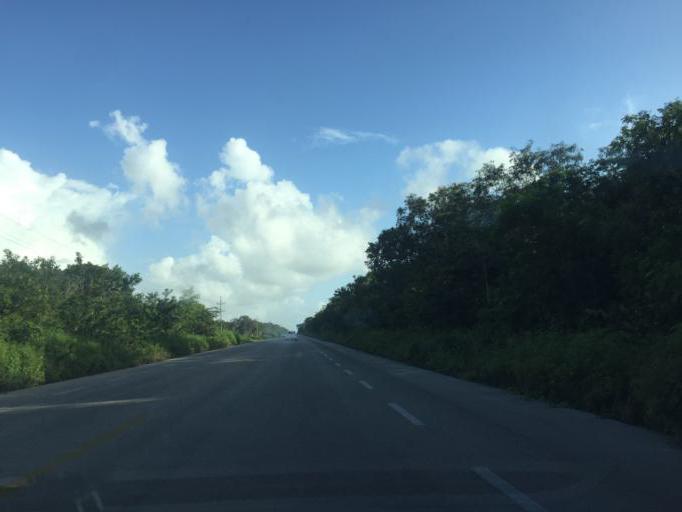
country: MX
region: Quintana Roo
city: Coba
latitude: 20.4911
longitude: -87.7039
